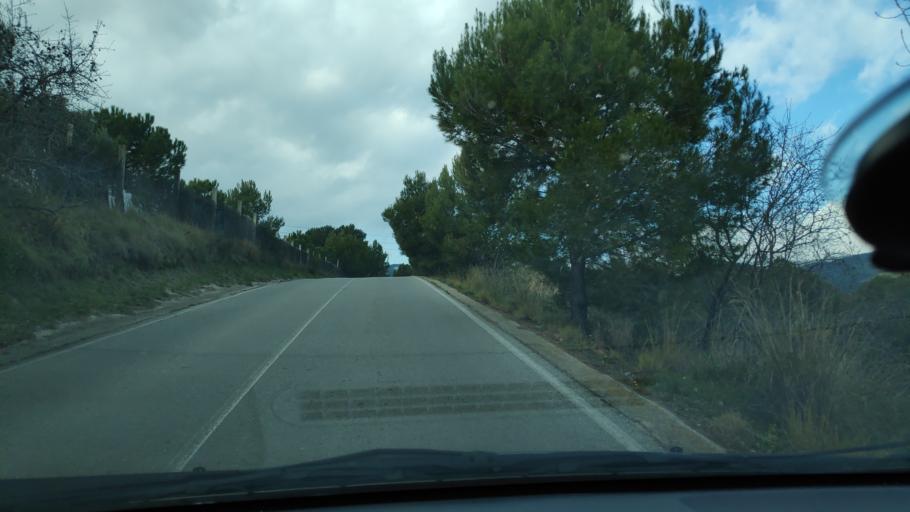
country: ES
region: Catalonia
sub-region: Provincia de Barcelona
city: Terrassa
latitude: 41.5749
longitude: 1.9881
